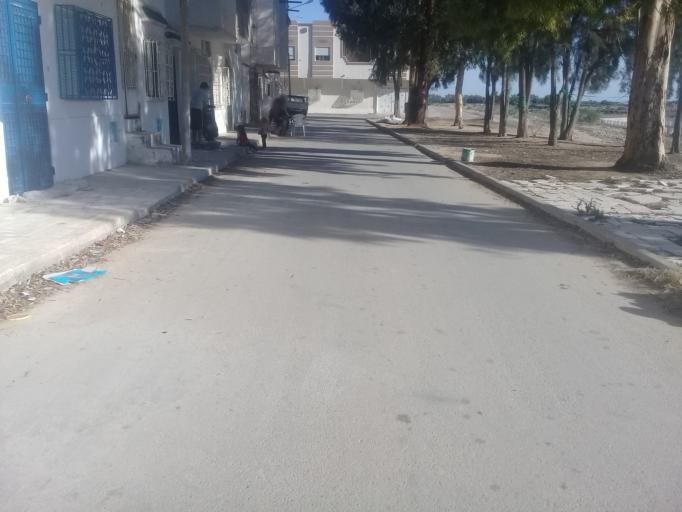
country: TN
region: Al Qayrawan
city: Kairouan
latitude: 35.6606
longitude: 10.1064
